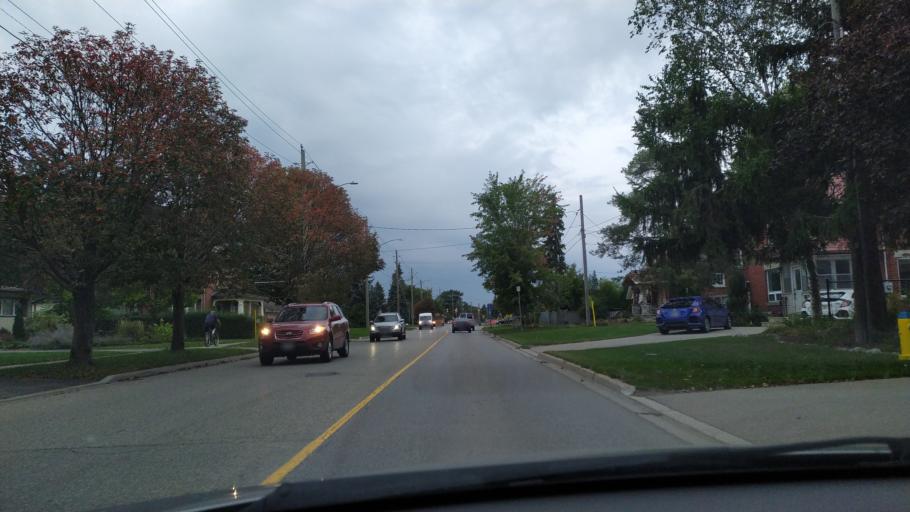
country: CA
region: Ontario
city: Waterloo
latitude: 43.4874
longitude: -80.4912
